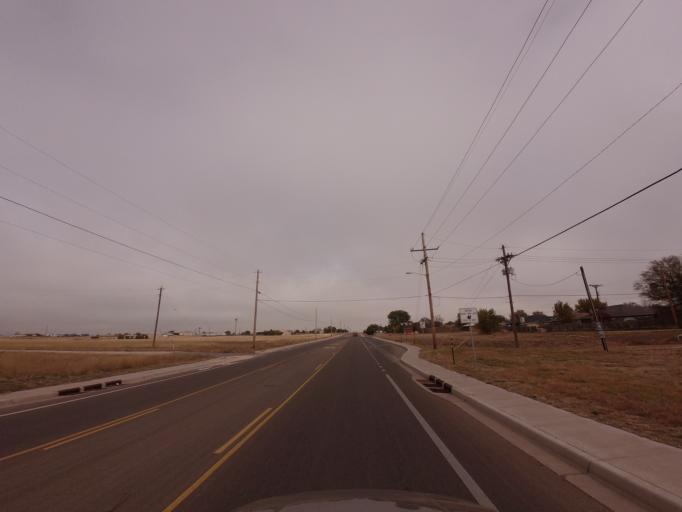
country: US
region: New Mexico
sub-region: Curry County
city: Clovis
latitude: 34.4259
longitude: -103.2317
